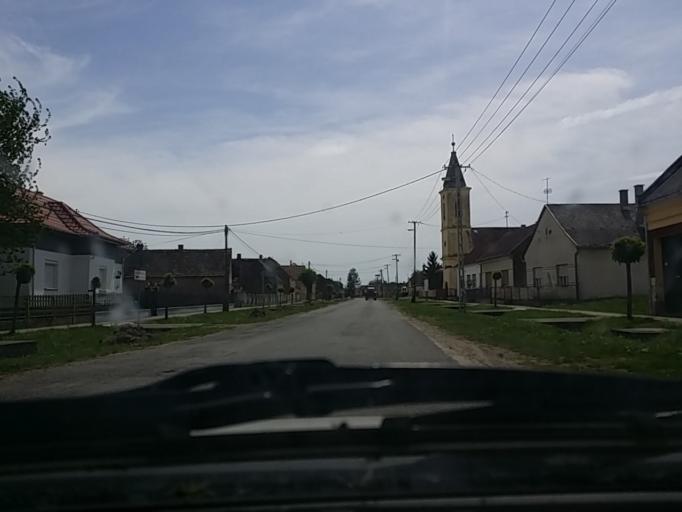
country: HU
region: Somogy
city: Barcs
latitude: 45.9548
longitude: 17.6168
